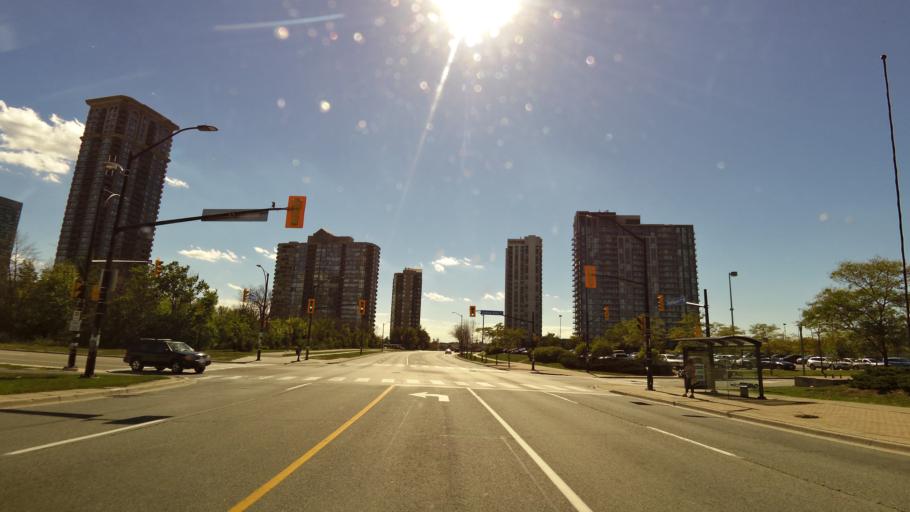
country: CA
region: Ontario
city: Mississauga
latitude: 43.5916
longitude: -79.6501
